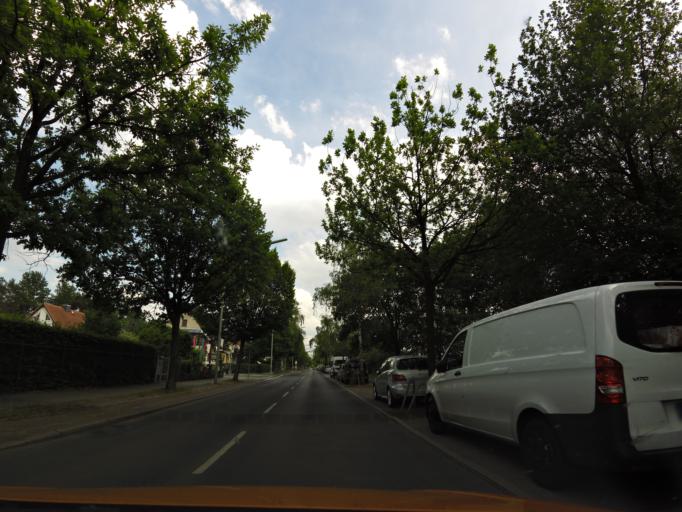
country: DE
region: Berlin
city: Heiligensee
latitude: 52.6056
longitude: 13.2321
